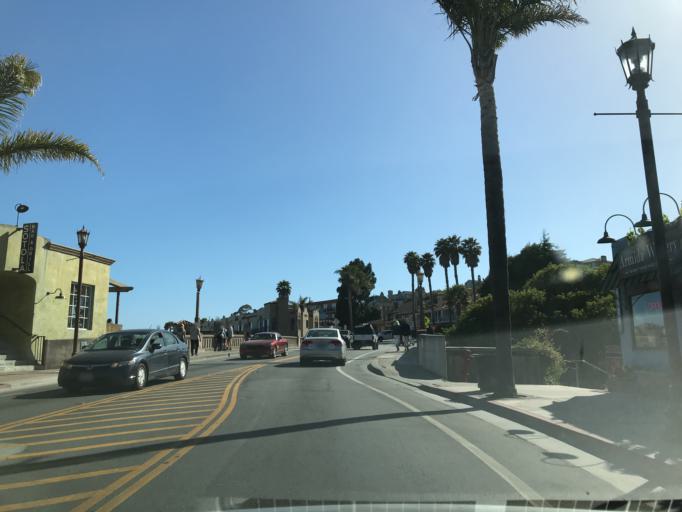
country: US
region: California
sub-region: Santa Cruz County
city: Capitola
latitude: 36.9727
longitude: -121.9526
